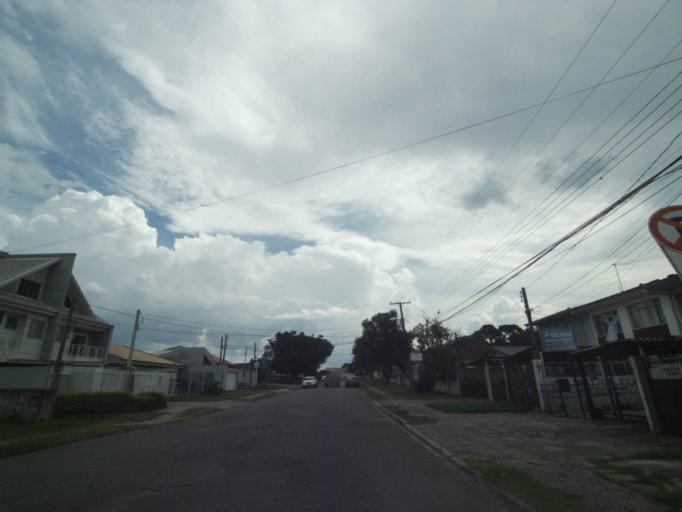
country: BR
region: Parana
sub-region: Pinhais
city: Pinhais
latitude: -25.4430
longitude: -49.2289
